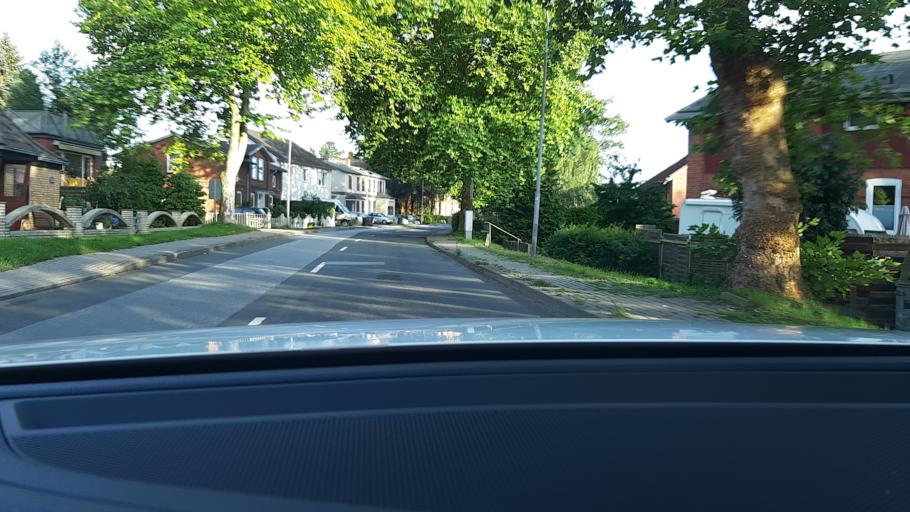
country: DE
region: Schleswig-Holstein
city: Stockelsdorf
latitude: 53.9009
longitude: 10.6443
